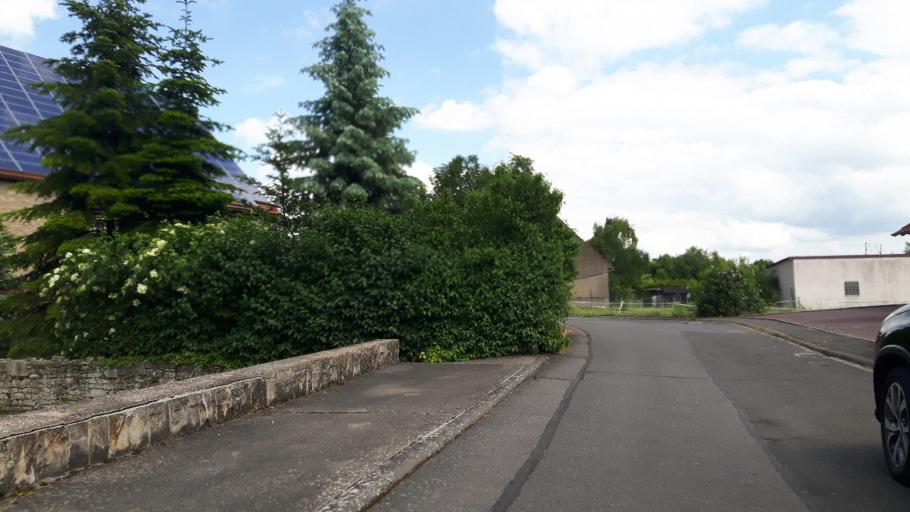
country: DE
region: Bavaria
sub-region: Regierungsbezirk Unterfranken
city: Butthard
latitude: 49.6108
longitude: 9.8392
